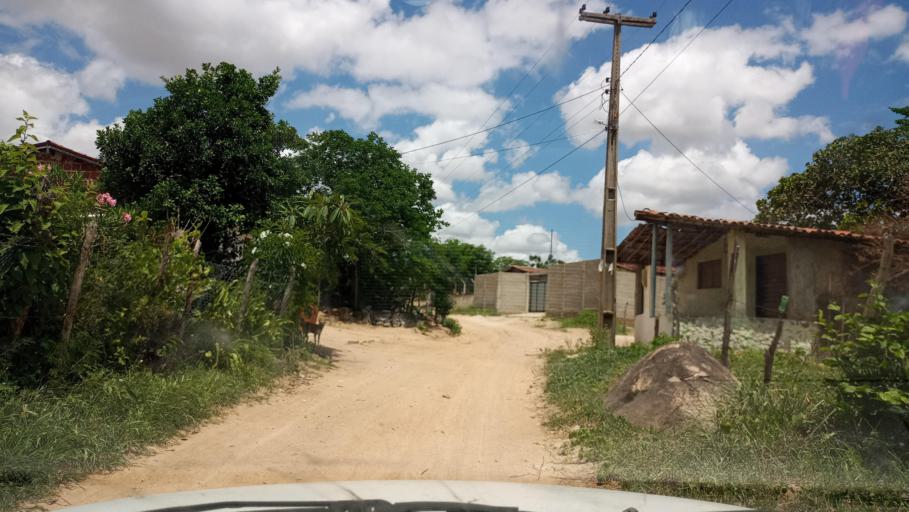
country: BR
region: Rio Grande do Norte
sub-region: Sao Jose Do Campestre
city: Sao Jose do Campestre
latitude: -6.4430
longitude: -35.6281
